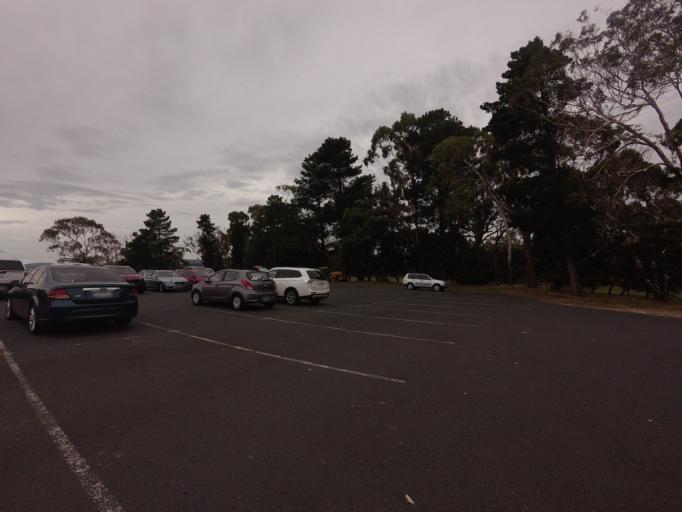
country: AU
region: Tasmania
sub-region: Clarence
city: Seven Mile Beach
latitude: -42.8180
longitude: 147.5068
